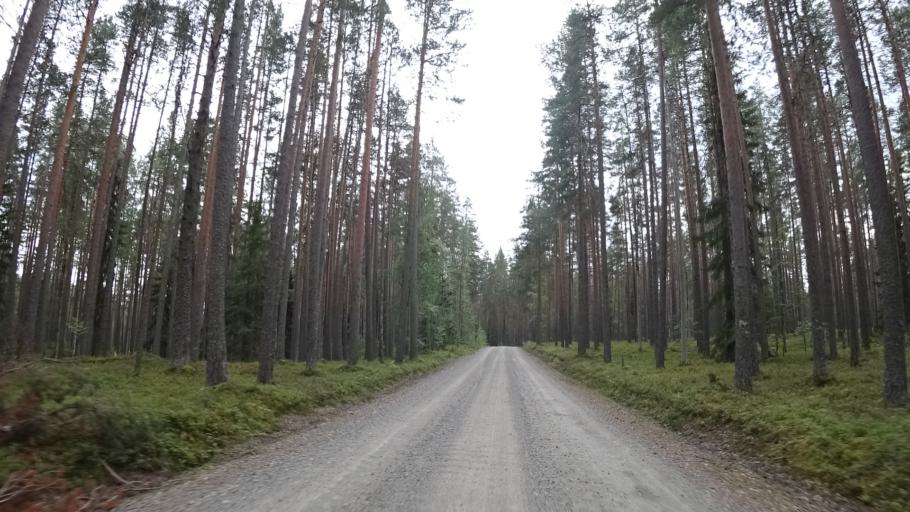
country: FI
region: North Karelia
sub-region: Joensuu
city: Ilomantsi
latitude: 62.5949
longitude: 31.1823
